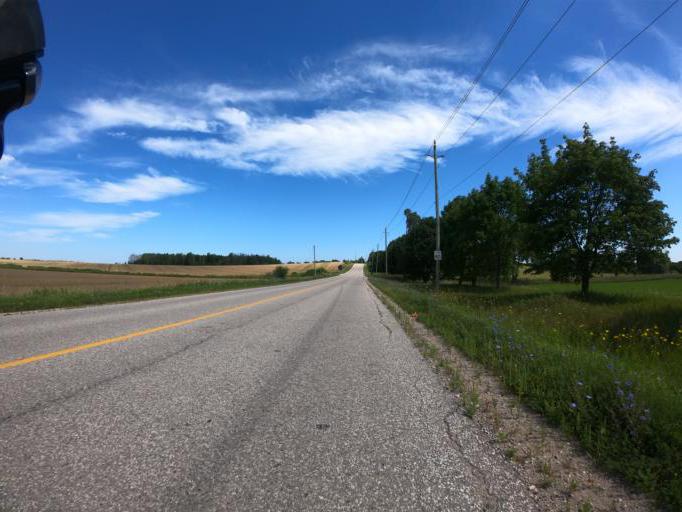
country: CA
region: Ontario
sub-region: Wellington County
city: Guelph
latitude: 43.5413
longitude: -80.3829
